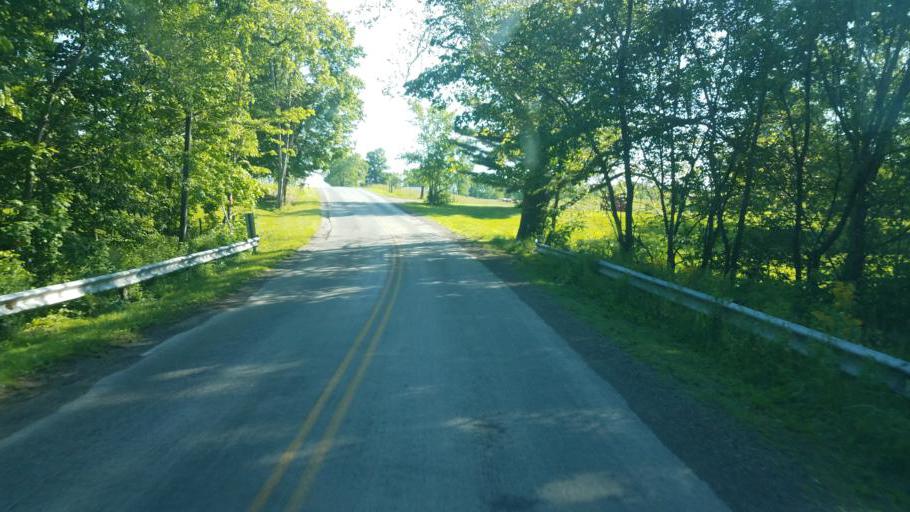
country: US
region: Ohio
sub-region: Hardin County
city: Kenton
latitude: 40.5839
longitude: -83.6237
